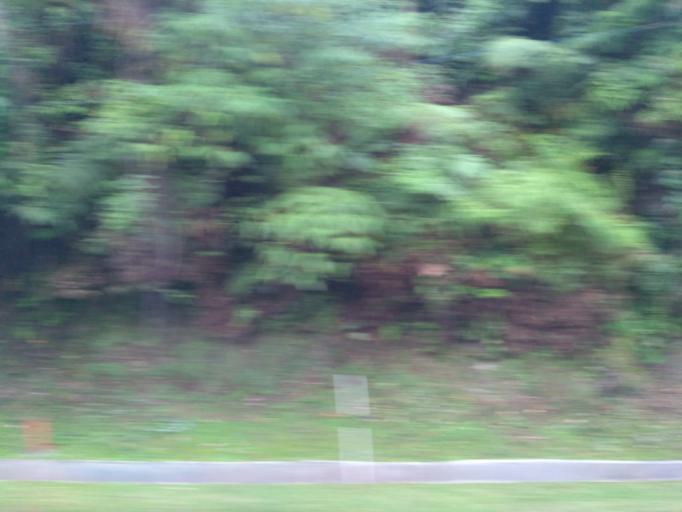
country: MY
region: Pahang
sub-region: Cameron Highlands
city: Tanah Rata
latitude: 4.4832
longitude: 101.3775
